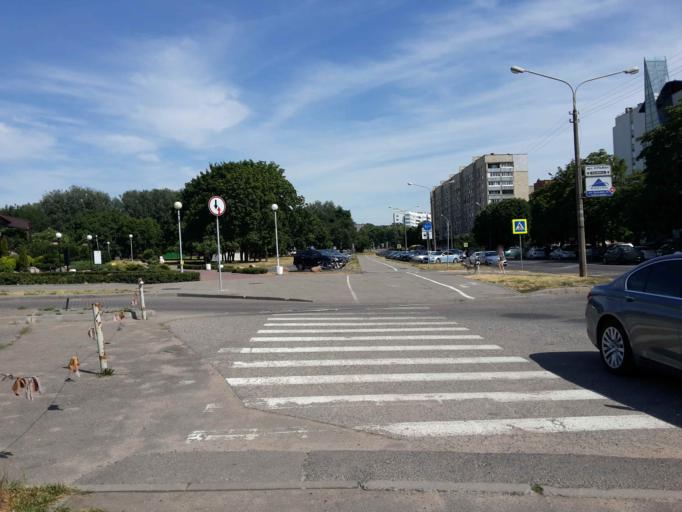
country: BY
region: Minsk
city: Minsk
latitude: 53.9278
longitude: 27.5672
